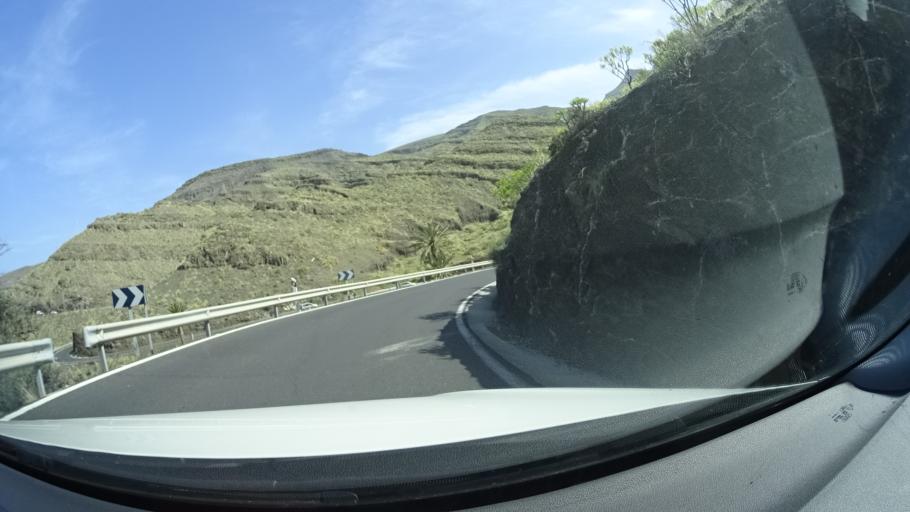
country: ES
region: Canary Islands
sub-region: Provincia de Las Palmas
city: Agaete
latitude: 28.0805
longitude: -15.7059
